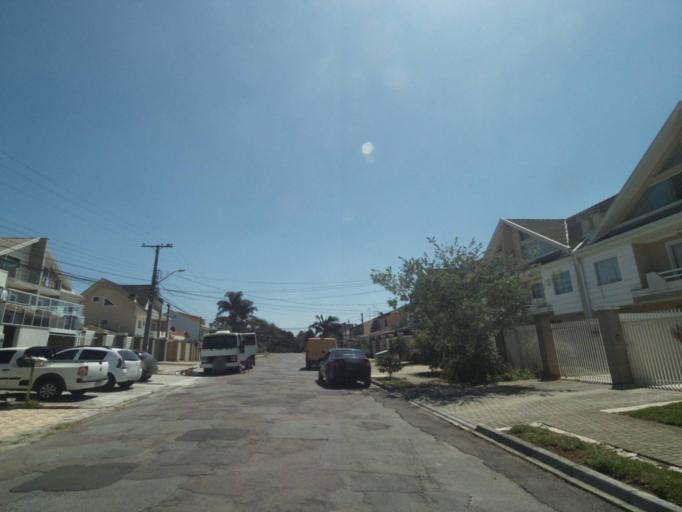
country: BR
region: Parana
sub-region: Sao Jose Dos Pinhais
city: Sao Jose dos Pinhais
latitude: -25.5122
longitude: -49.2434
